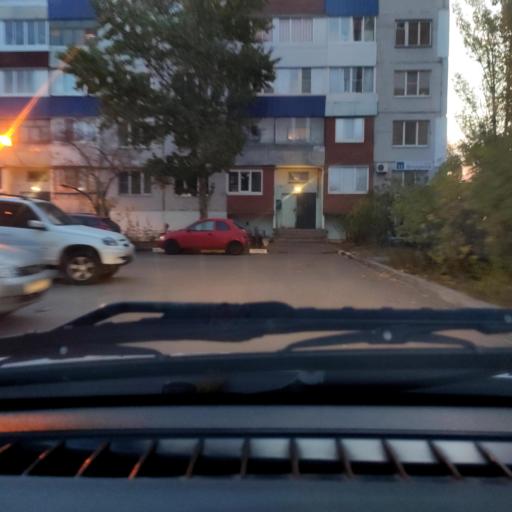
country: RU
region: Samara
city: Zhigulevsk
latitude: 53.4774
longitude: 49.4849
